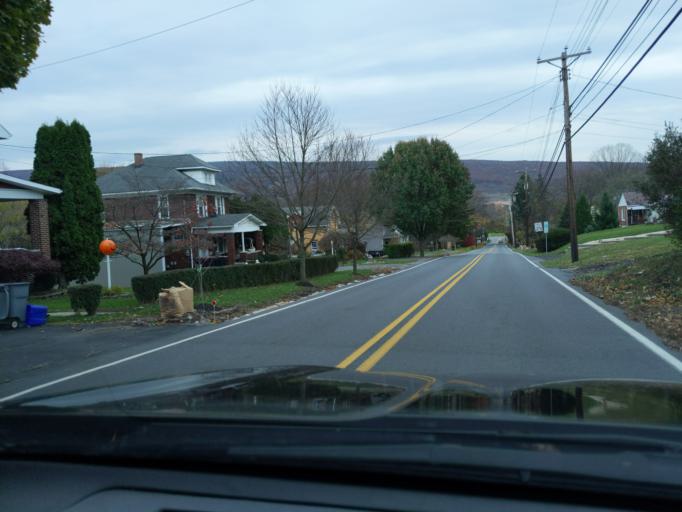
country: US
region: Pennsylvania
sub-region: Blair County
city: Altoona
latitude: 40.4996
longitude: -78.3976
